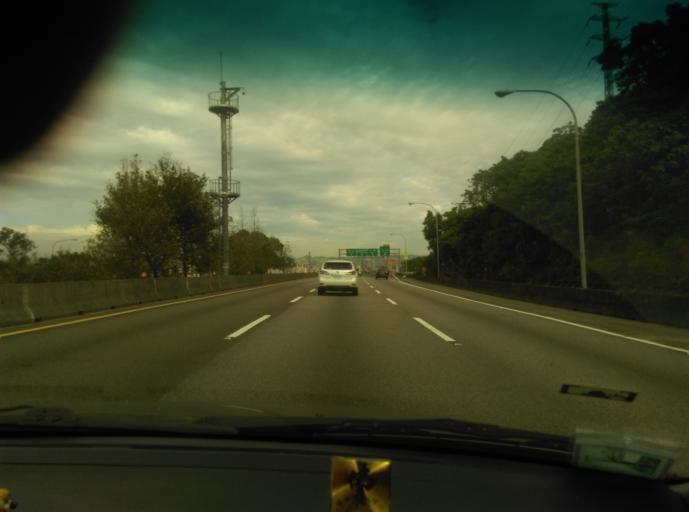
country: TW
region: Taipei
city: Taipei
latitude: 24.9634
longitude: 121.5458
